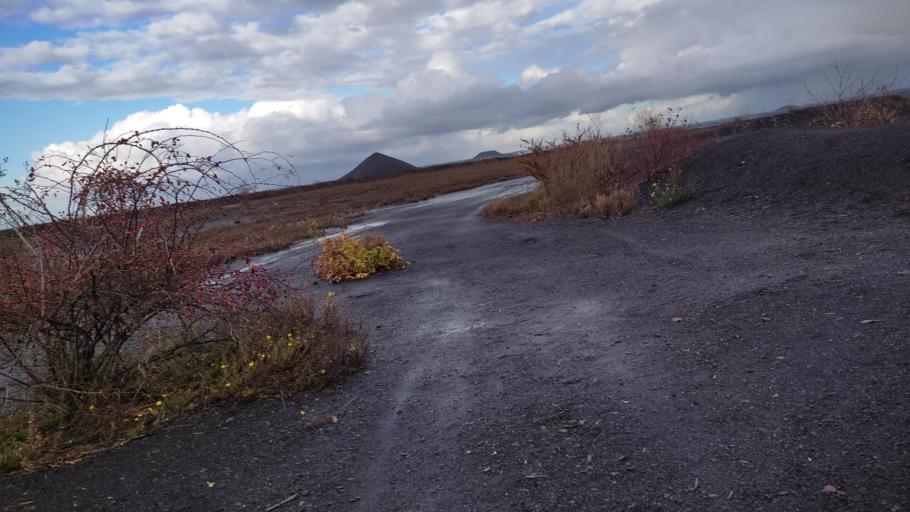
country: FR
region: Nord-Pas-de-Calais
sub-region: Departement du Pas-de-Calais
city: Noyelles-sous-Lens
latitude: 50.4351
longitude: 2.8826
